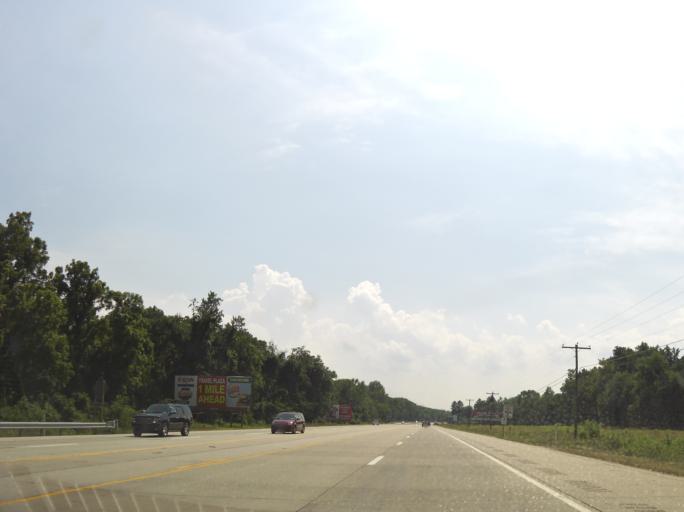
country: US
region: Pennsylvania
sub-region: Dauphin County
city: Matamoras
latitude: 40.4607
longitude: -76.9574
